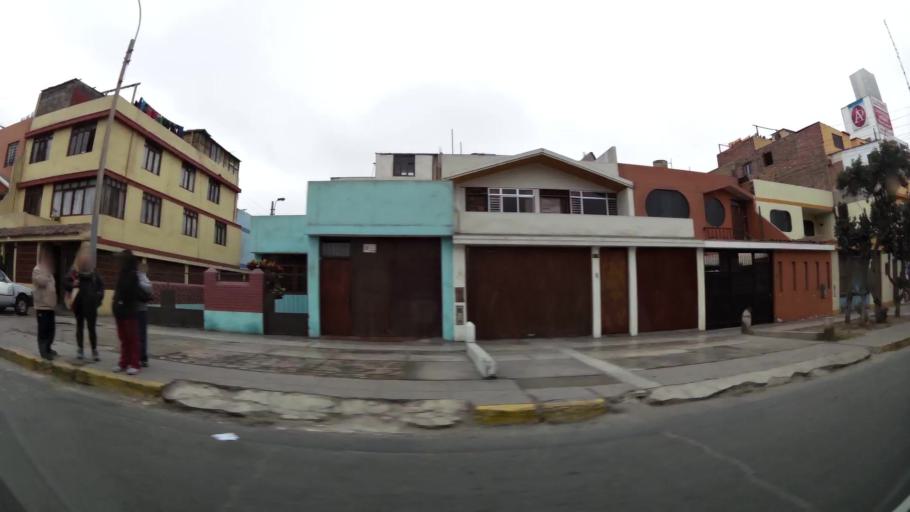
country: PE
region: Callao
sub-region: Callao
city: Callao
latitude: -12.0816
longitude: -77.1020
